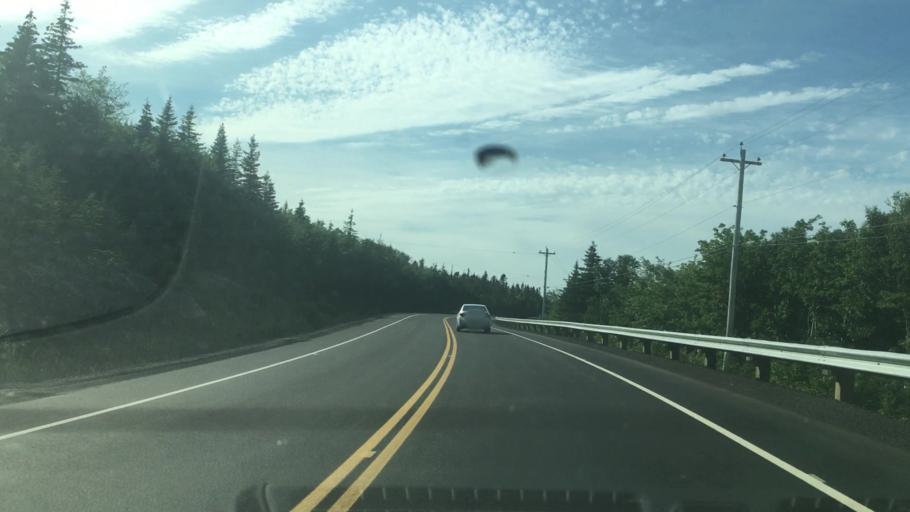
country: CA
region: Nova Scotia
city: Sydney Mines
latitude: 46.8402
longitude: -60.3893
